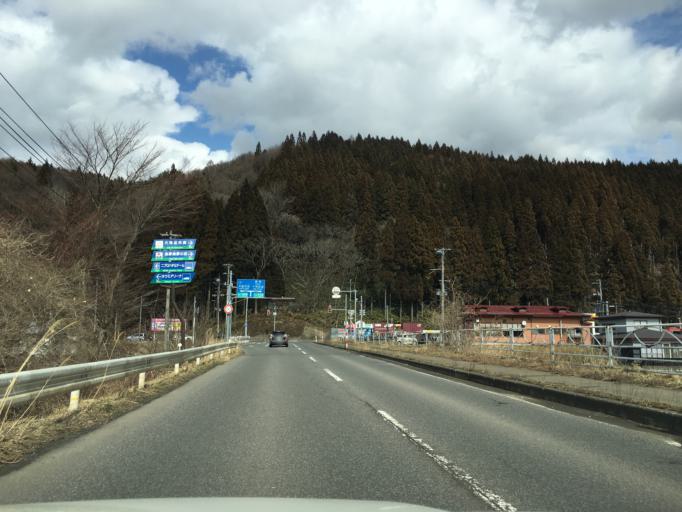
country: JP
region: Akita
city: Odate
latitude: 40.2296
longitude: 140.5920
